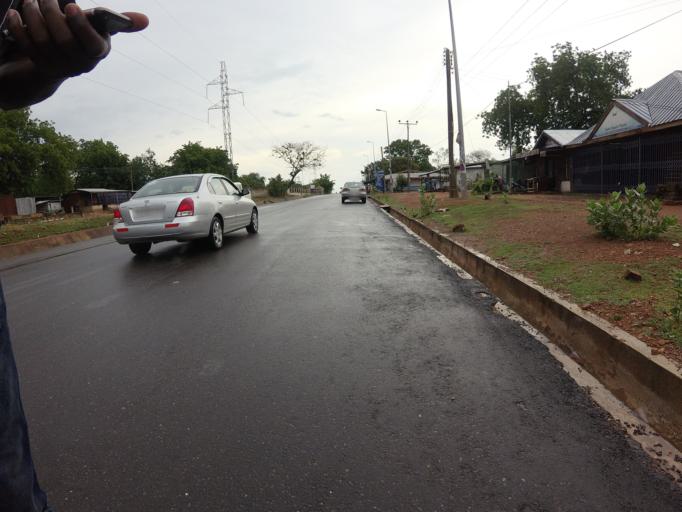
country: GH
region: Upper East
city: Bolgatanga
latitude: 10.7926
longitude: -0.8569
